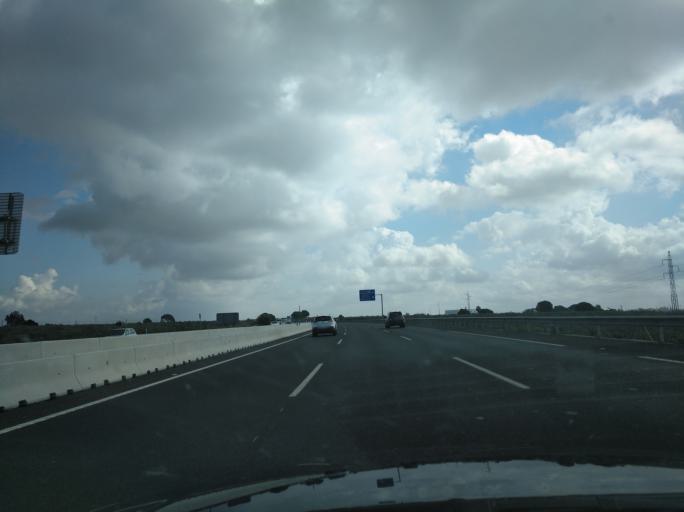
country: ES
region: Andalusia
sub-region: Provincia de Sevilla
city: Benacazon
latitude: 37.3581
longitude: -6.1904
